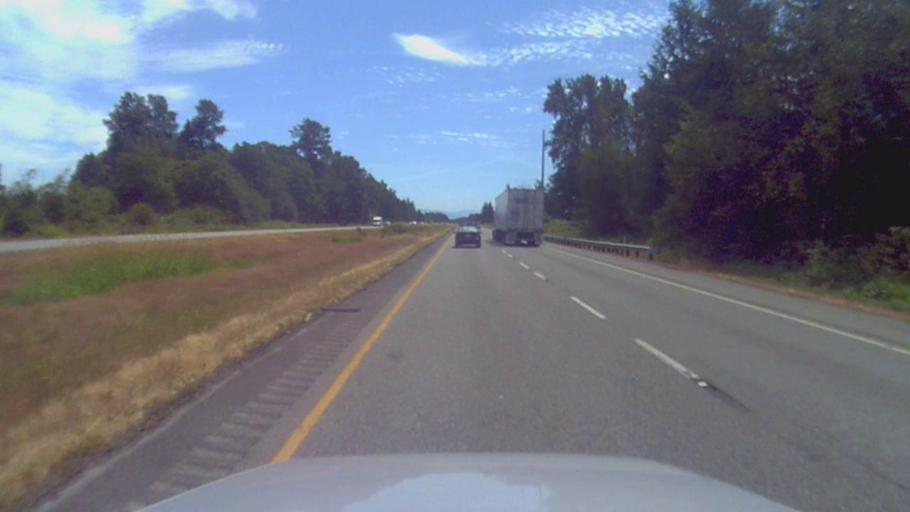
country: US
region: Washington
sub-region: Whatcom County
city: Ferndale
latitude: 48.9013
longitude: -122.6126
